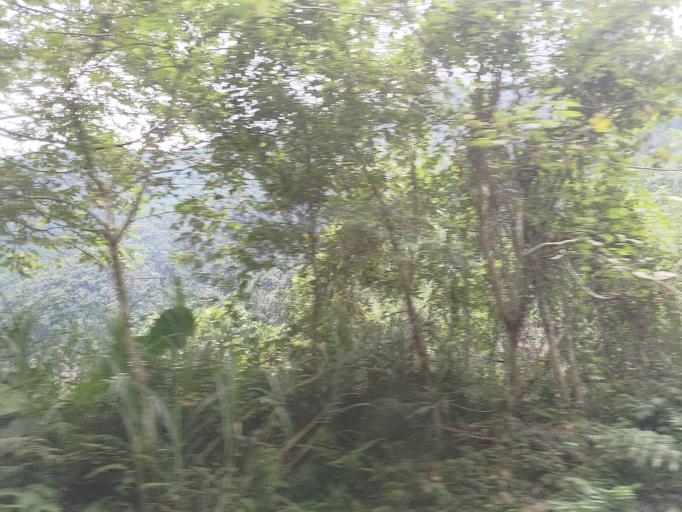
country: TW
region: Taiwan
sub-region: Hsinchu
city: Hsinchu
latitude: 24.6153
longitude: 121.0927
